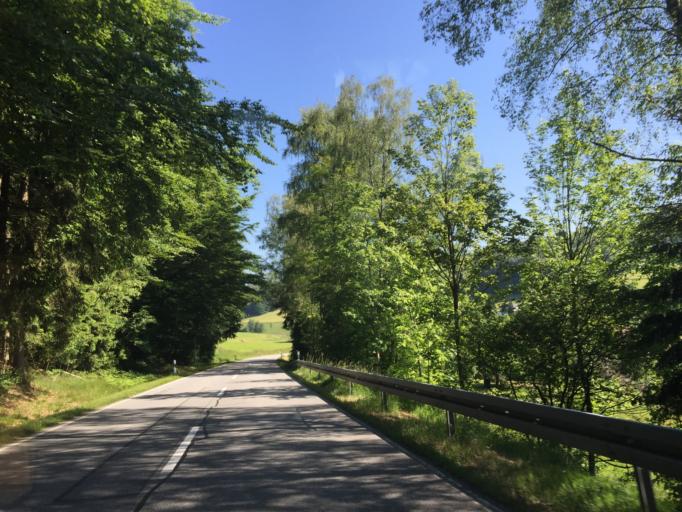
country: DE
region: Hesse
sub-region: Regierungsbezirk Darmstadt
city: Wald-Michelbach
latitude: 49.5969
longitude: 8.8919
